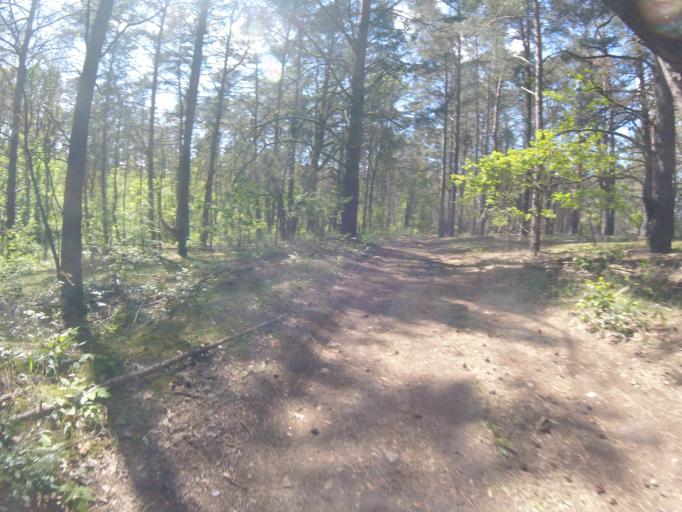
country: DE
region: Brandenburg
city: Teupitz
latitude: 52.1343
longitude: 13.5815
